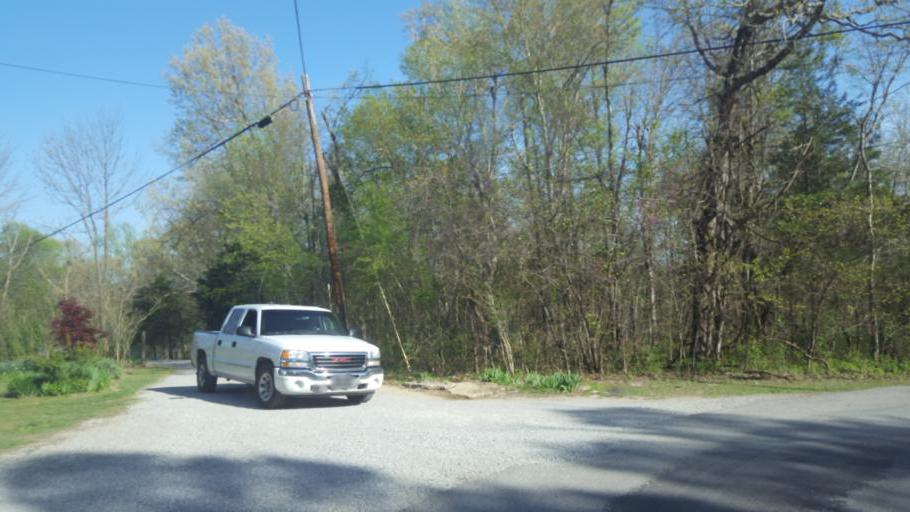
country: US
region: Kentucky
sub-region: Barren County
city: Cave City
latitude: 37.1757
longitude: -86.0312
